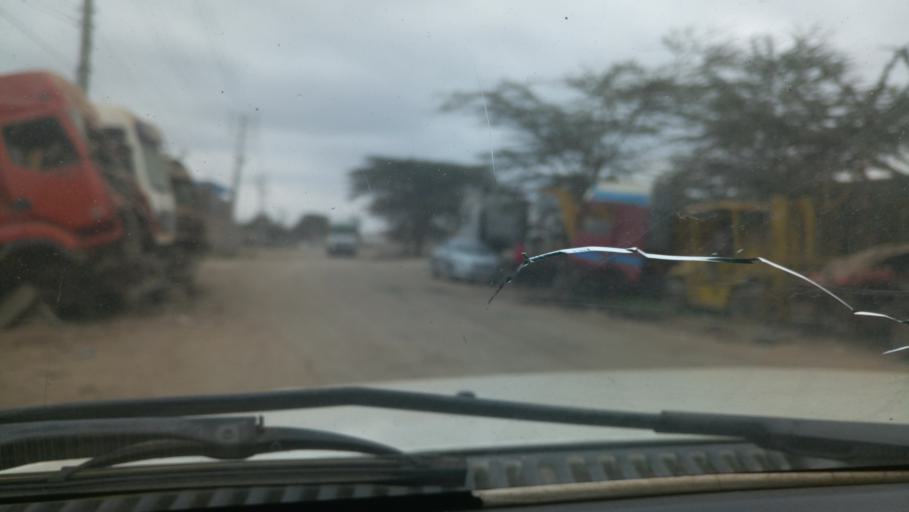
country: KE
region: Nairobi Area
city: Pumwani
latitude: -1.3348
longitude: 36.8661
